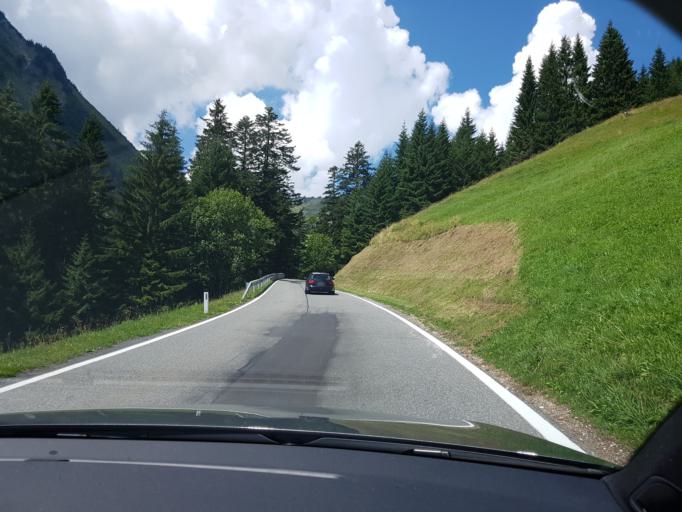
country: AT
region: Vorarlberg
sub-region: Politischer Bezirk Bregenz
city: Damuels
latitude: 47.2607
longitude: 9.9135
